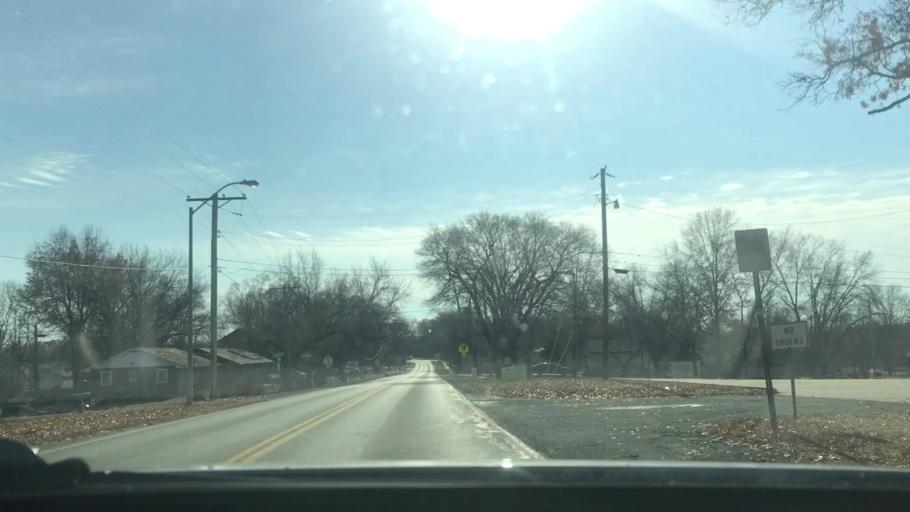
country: US
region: Missouri
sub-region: Clay County
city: Smithville
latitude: 39.3011
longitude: -94.5800
